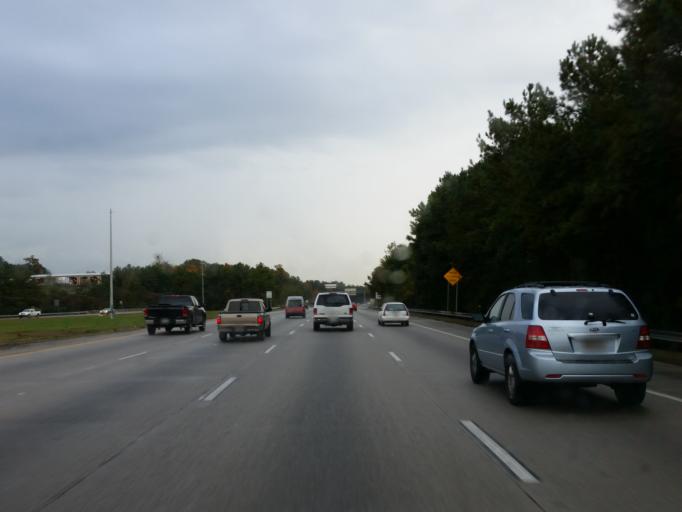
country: US
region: Georgia
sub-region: Clayton County
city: Conley
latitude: 33.6688
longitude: -84.3267
